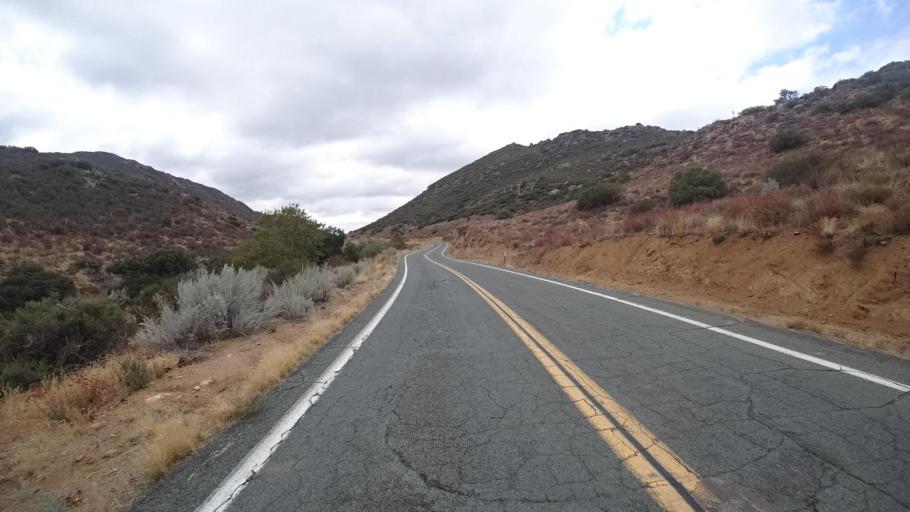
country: US
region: California
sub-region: San Diego County
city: Pine Valley
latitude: 32.7646
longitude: -116.4520
